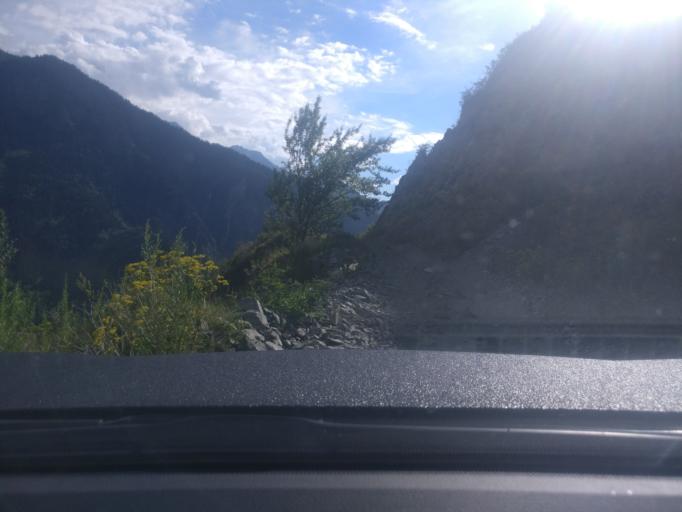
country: KZ
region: Almaty Qalasy
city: Almaty
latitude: 43.1070
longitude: 76.9493
